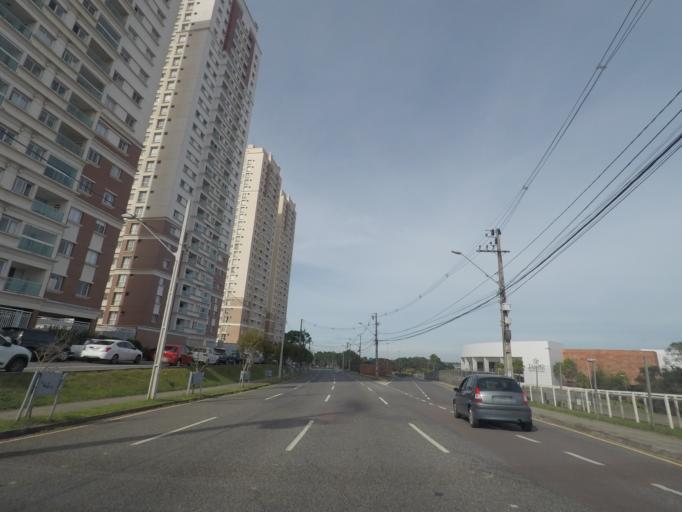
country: BR
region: Parana
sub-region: Curitiba
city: Curitiba
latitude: -25.4451
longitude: -49.3555
